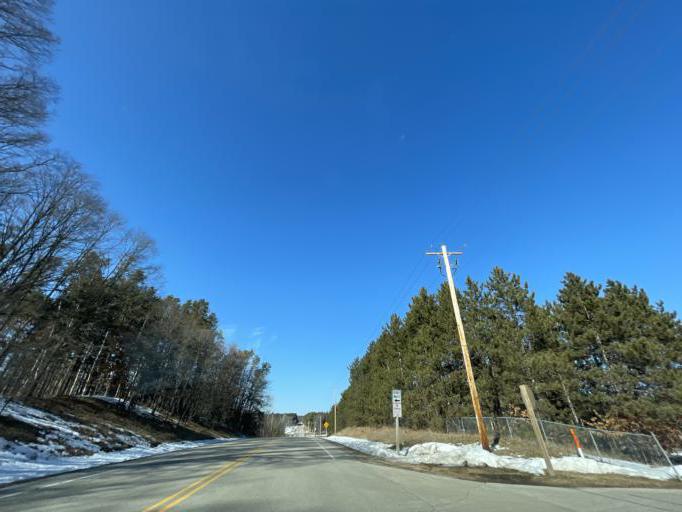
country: US
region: Wisconsin
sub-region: Brown County
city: Suamico
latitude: 44.6568
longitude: -88.0903
